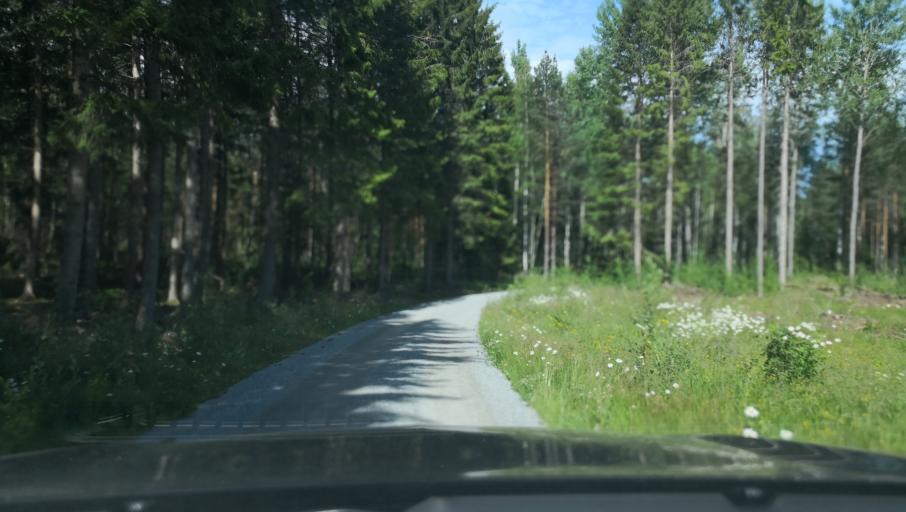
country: SE
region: Vaestmanland
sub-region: Surahammars Kommun
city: Ramnas
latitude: 59.9455
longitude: 16.1914
